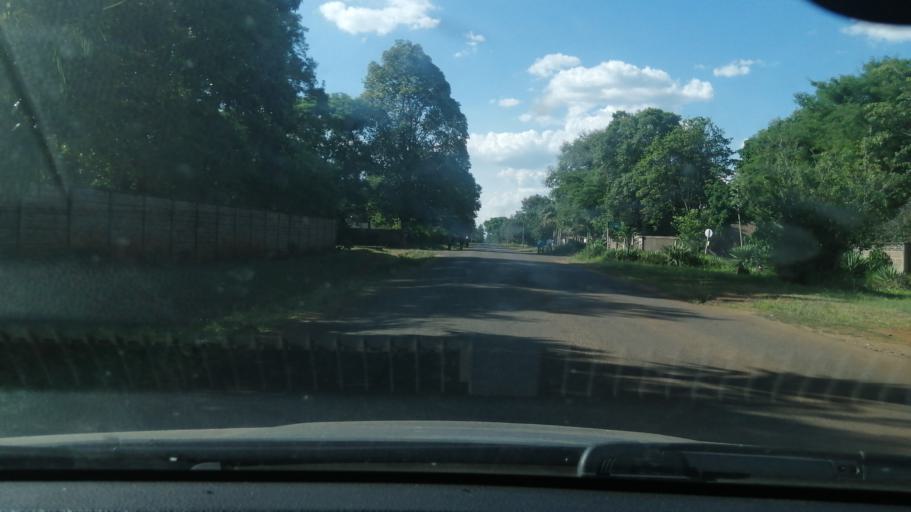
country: ZW
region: Harare
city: Harare
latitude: -17.7652
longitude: 31.0566
